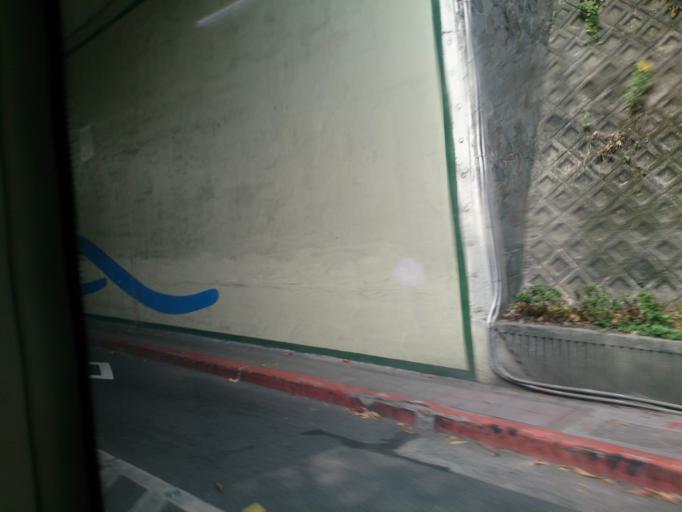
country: TW
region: Taipei
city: Taipei
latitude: 25.0769
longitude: 121.5260
